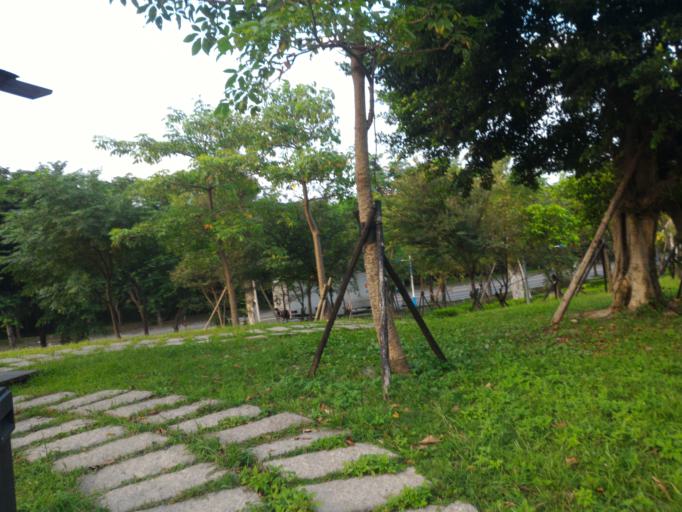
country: TW
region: Taiwan
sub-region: Taoyuan
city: Taoyuan
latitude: 24.9509
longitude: 121.3851
